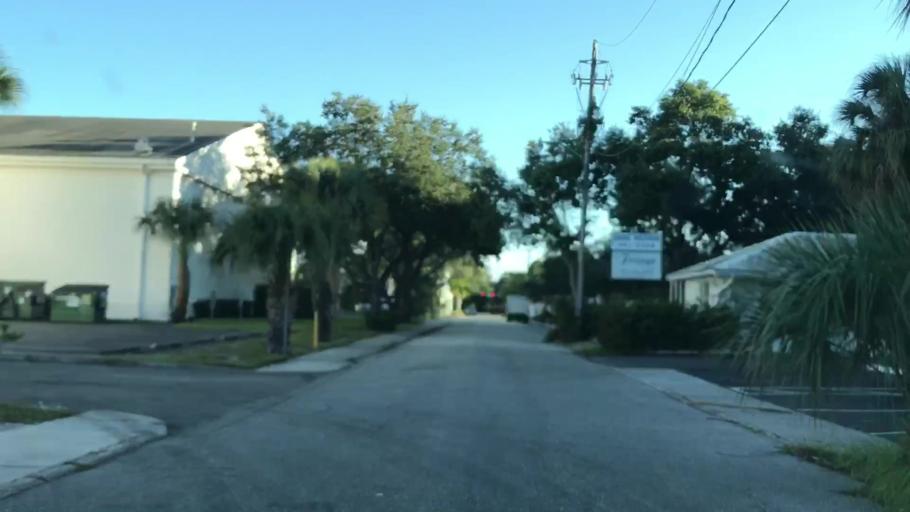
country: US
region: Florida
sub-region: Sarasota County
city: Sarasota
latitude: 27.3366
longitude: -82.5361
